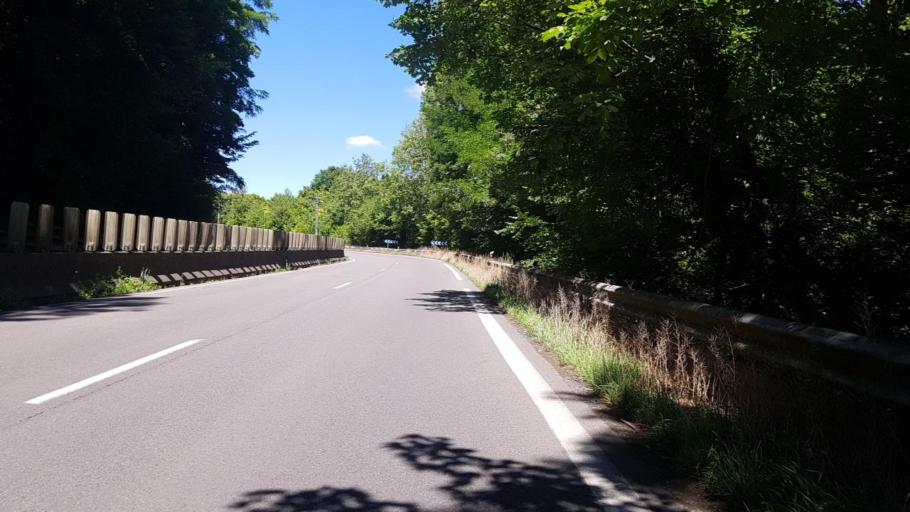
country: FR
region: Ile-de-France
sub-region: Departement de Seine-et-Marne
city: Saint-Jean-les-Deux-Jumeaux
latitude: 48.9584
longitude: 3.0027
